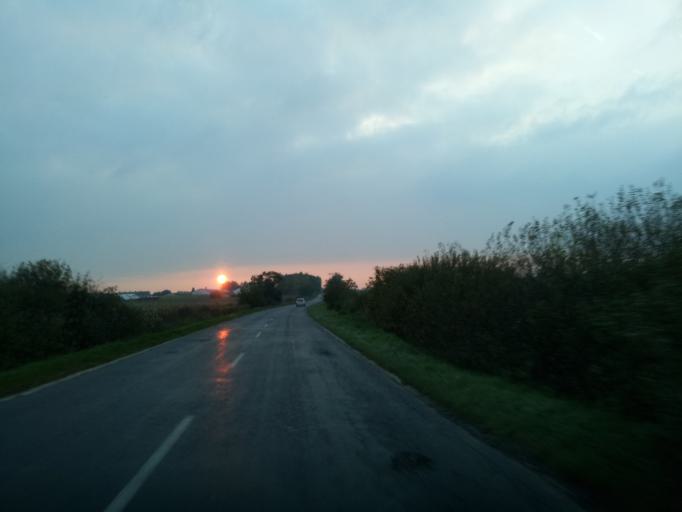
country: HU
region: Gyor-Moson-Sopron
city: Bakonyszentlaszlo
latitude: 47.4437
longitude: 17.8044
